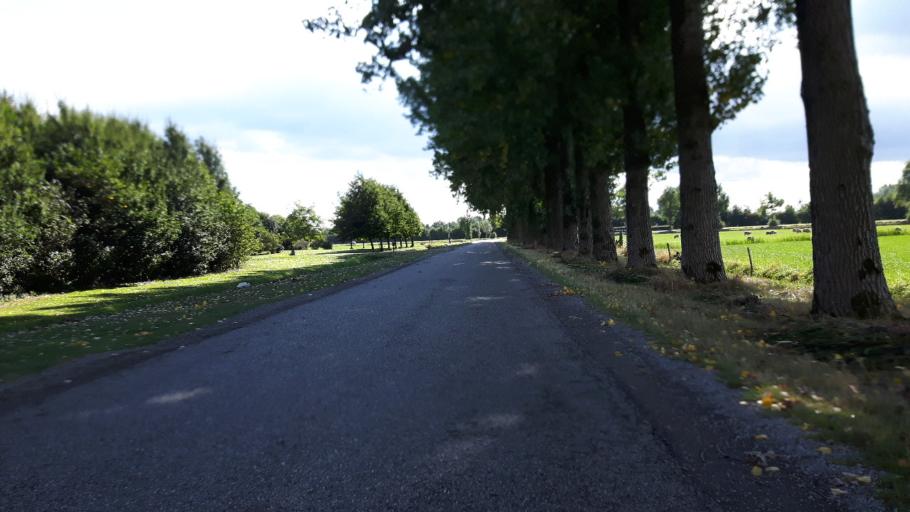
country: NL
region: South Holland
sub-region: Gemeente Leerdam
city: Leerdam
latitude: 51.8884
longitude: 5.1309
